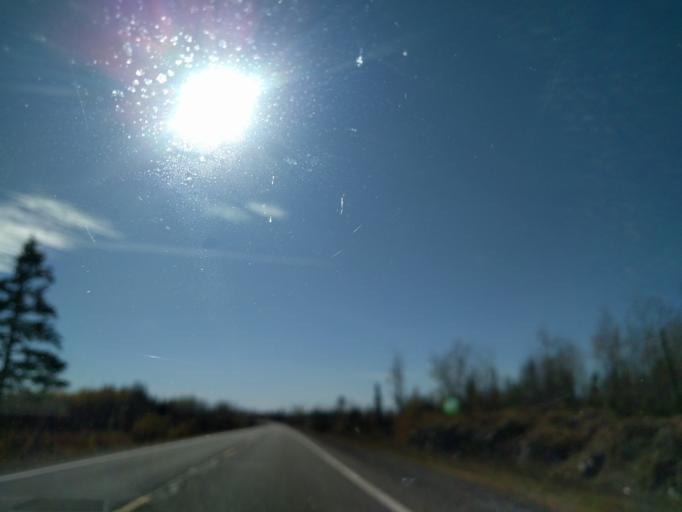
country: US
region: Michigan
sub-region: Marquette County
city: West Ishpeming
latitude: 46.4418
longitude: -87.9605
